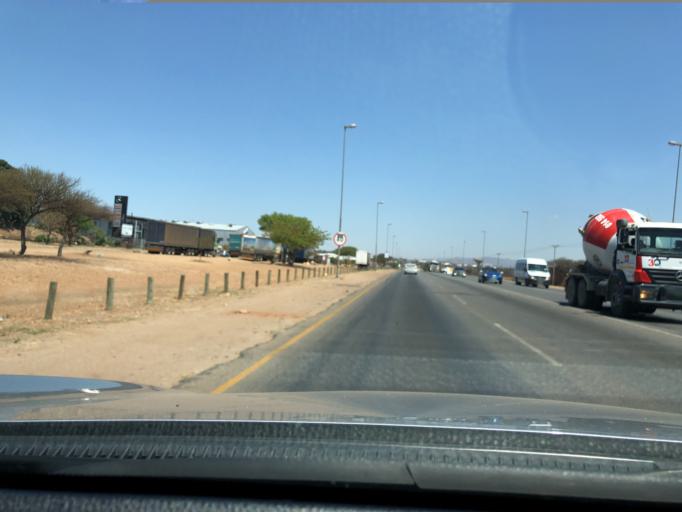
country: ZA
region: Limpopo
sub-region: Capricorn District Municipality
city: Polokwane
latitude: -23.8628
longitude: 29.4700
